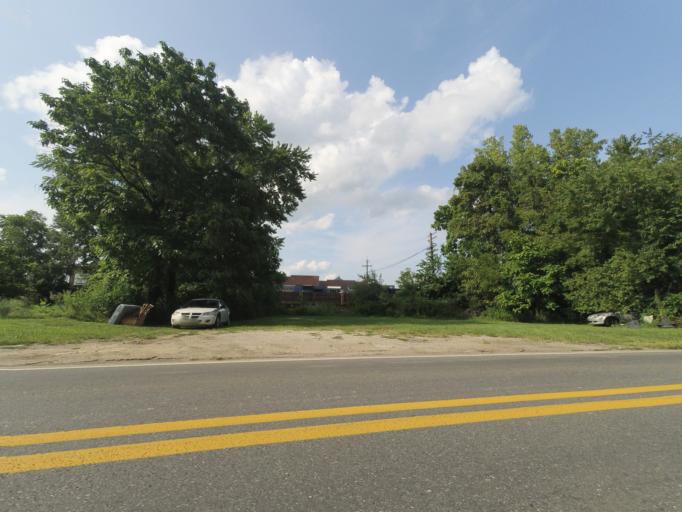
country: US
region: West Virginia
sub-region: Cabell County
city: Huntington
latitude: 38.4212
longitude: -82.4085
